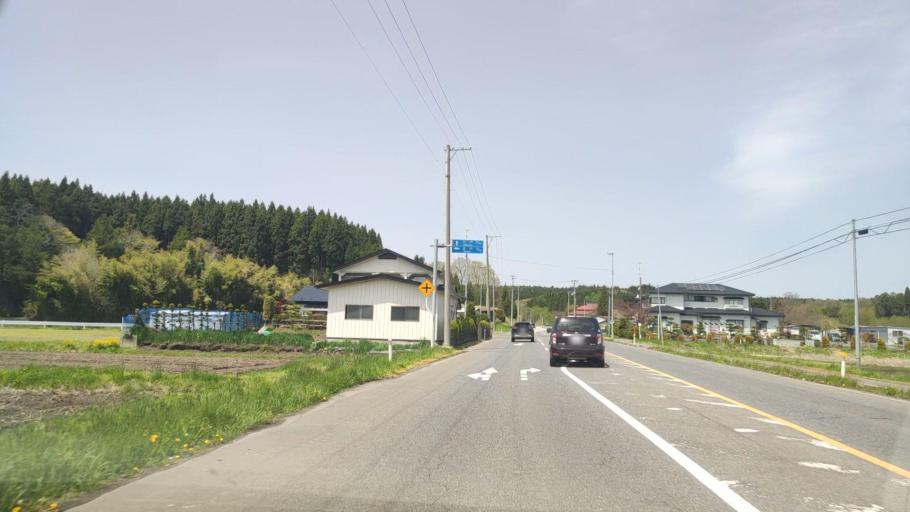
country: JP
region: Aomori
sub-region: Misawa Shi
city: Inuotose
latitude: 40.5600
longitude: 141.3851
